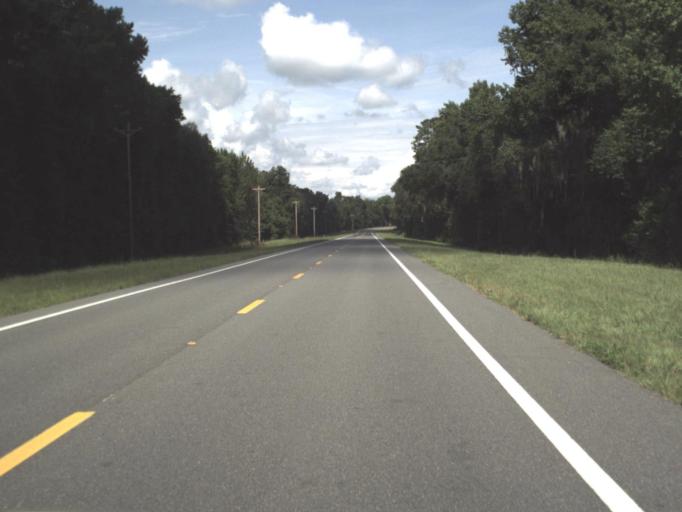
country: US
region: Florida
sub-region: Alachua County
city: Alachua
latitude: 29.8400
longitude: -82.3765
